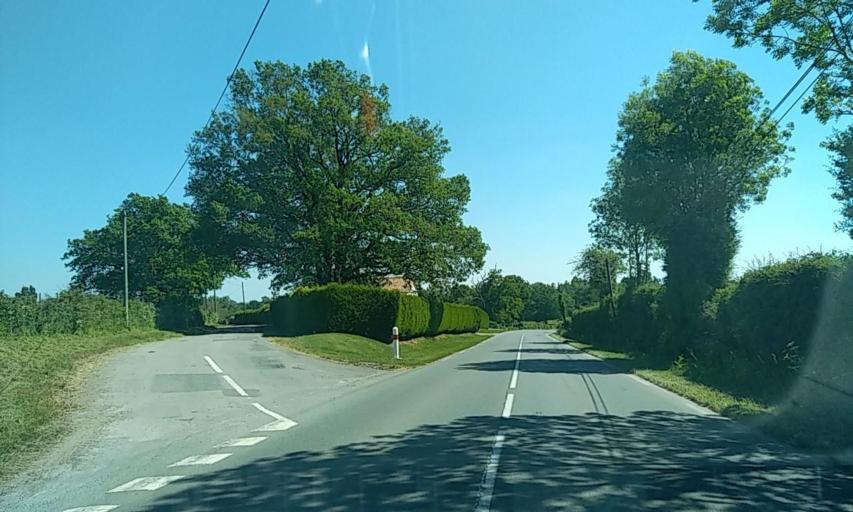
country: FR
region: Poitou-Charentes
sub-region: Departement des Deux-Sevres
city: La Chapelle-Saint-Laurent
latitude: 46.7875
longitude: -0.4793
